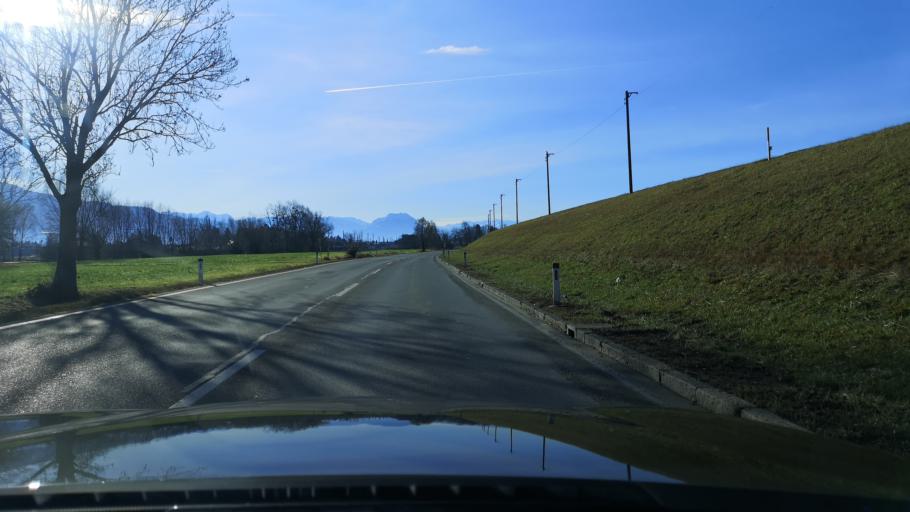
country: AT
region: Vorarlberg
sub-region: Politischer Bezirk Bregenz
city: Fussach
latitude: 47.4578
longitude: 9.6696
